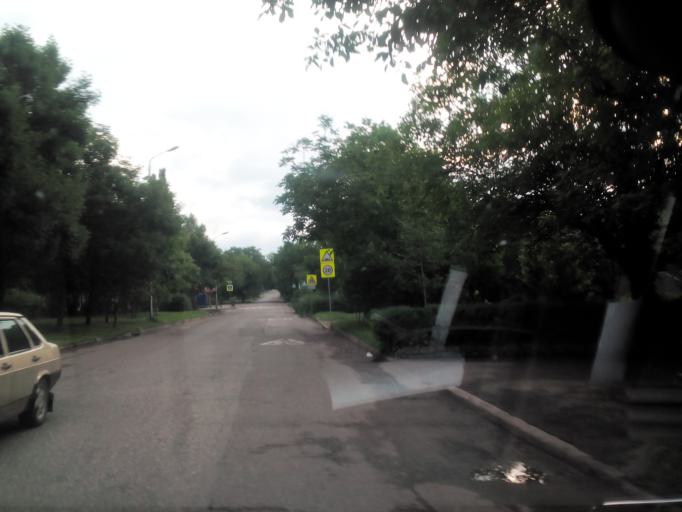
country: RU
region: Stavropol'skiy
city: Pyatigorsk
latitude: 44.0507
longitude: 43.0448
